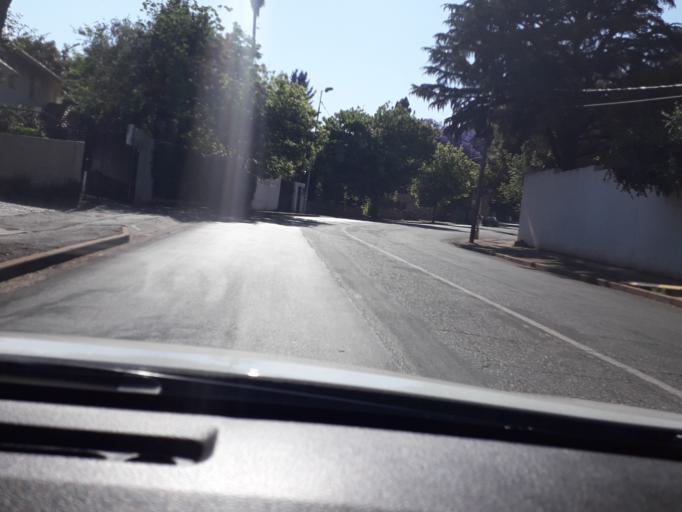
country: ZA
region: Gauteng
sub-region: City of Johannesburg Metropolitan Municipality
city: Johannesburg
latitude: -26.1787
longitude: 28.0250
